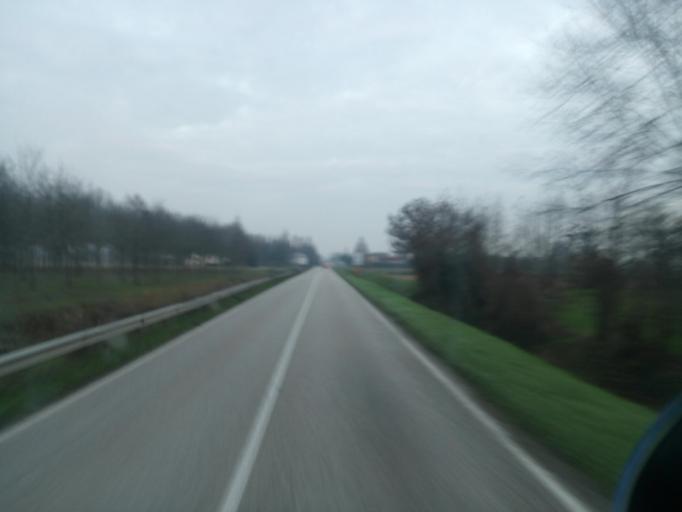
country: IT
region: Lombardy
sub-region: Provincia di Mantova
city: Stradella
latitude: 45.1718
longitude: 10.8623
